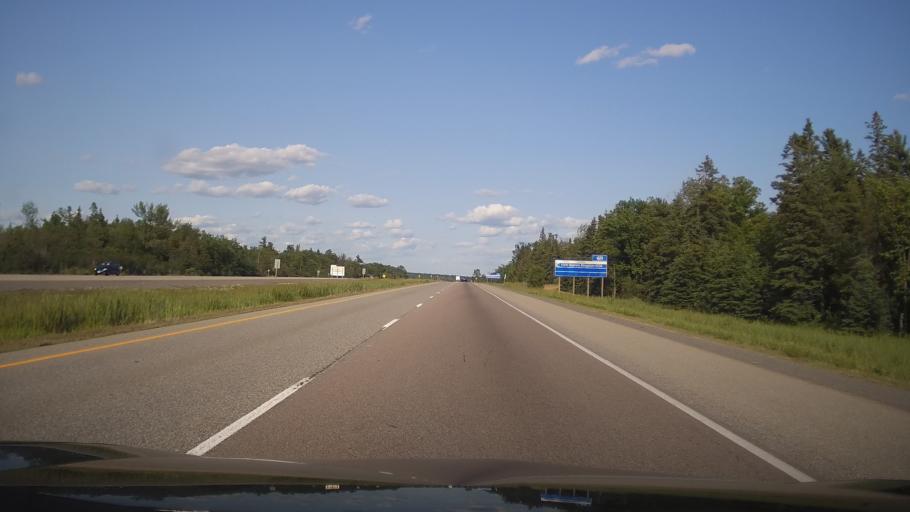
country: CA
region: Ontario
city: Kingston
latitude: 44.2872
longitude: -76.6042
